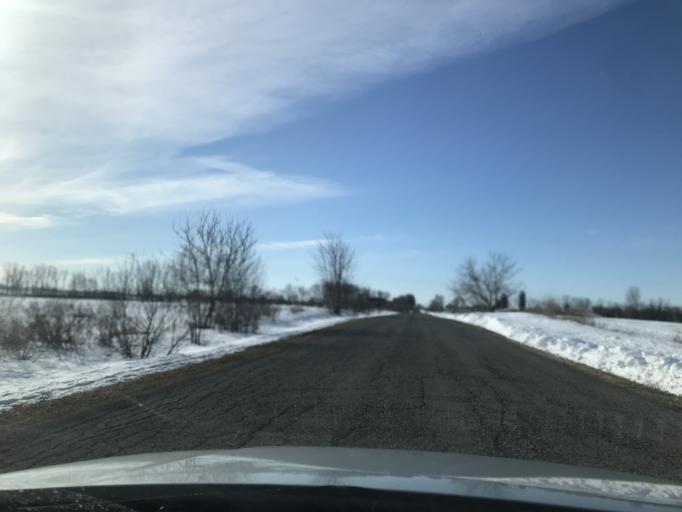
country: US
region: Wisconsin
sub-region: Oconto County
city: Oconto Falls
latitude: 44.9464
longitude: -88.0165
